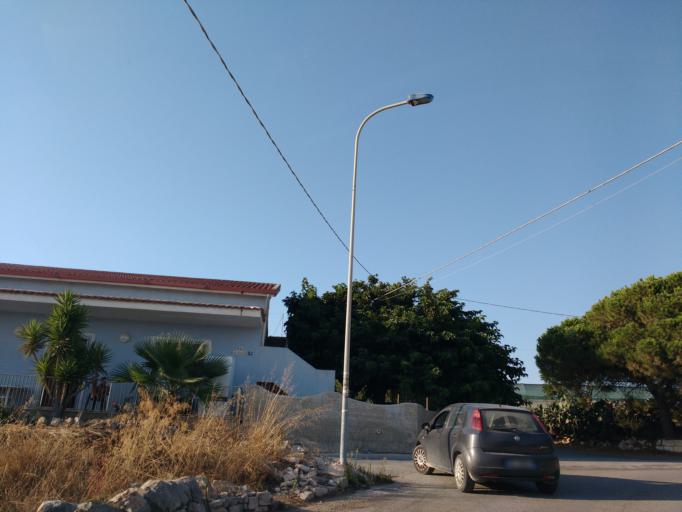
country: IT
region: Sicily
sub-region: Ragusa
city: Cava d'Aliga
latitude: 36.7317
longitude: 14.6938
